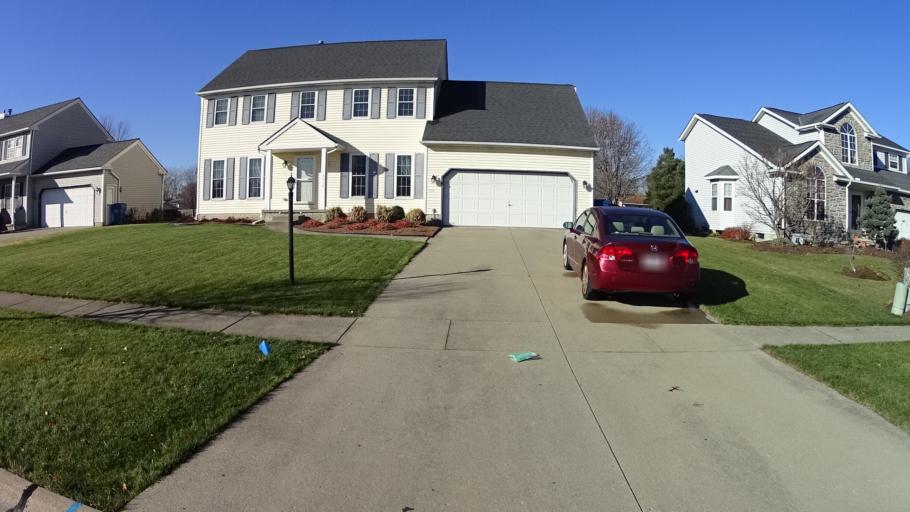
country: US
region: Ohio
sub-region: Lorain County
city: North Ridgeville
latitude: 41.4136
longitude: -82.0120
